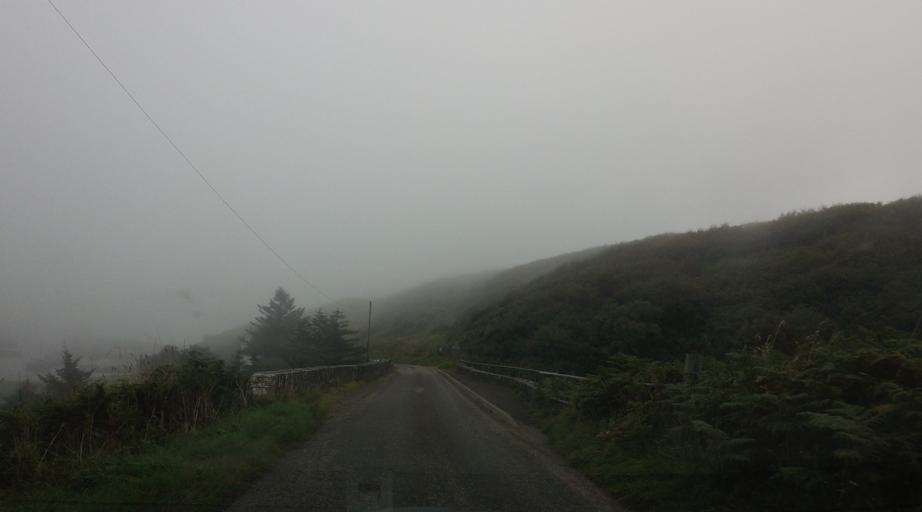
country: GB
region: Scotland
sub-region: Highland
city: Wick
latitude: 58.2981
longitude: -3.2925
